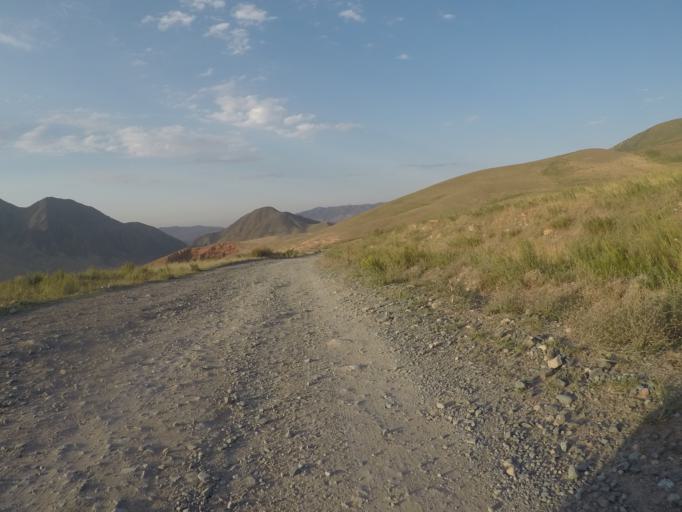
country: KG
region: Chuy
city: Bishkek
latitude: 42.6567
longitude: 74.6521
